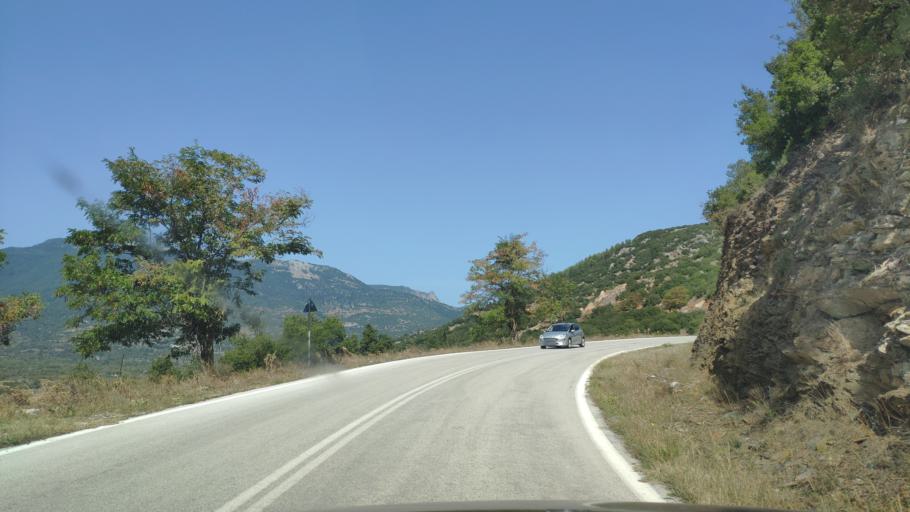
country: GR
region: West Greece
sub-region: Nomos Achaias
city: Aiyira
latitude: 37.9191
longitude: 22.3376
